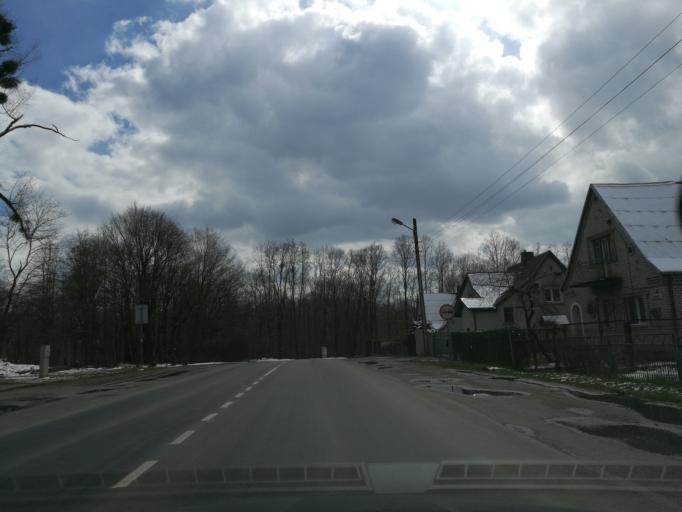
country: LT
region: Kauno apskritis
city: Dainava (Kaunas)
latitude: 54.8639
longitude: 24.0004
